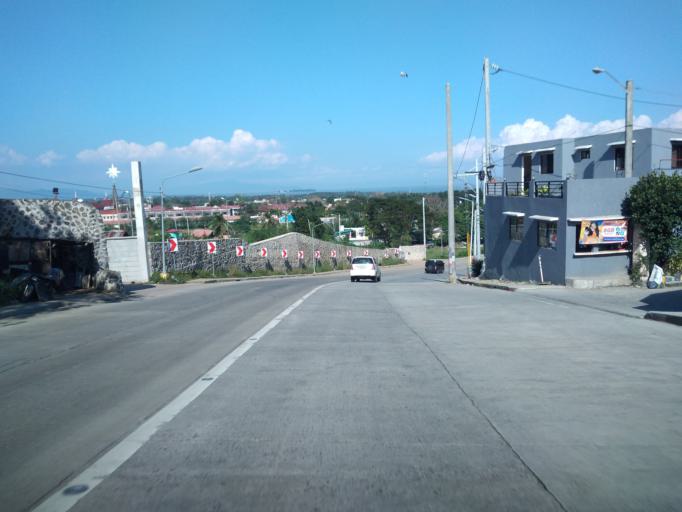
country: PH
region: Calabarzon
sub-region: Province of Laguna
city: Calamba
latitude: 14.1853
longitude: 121.1625
